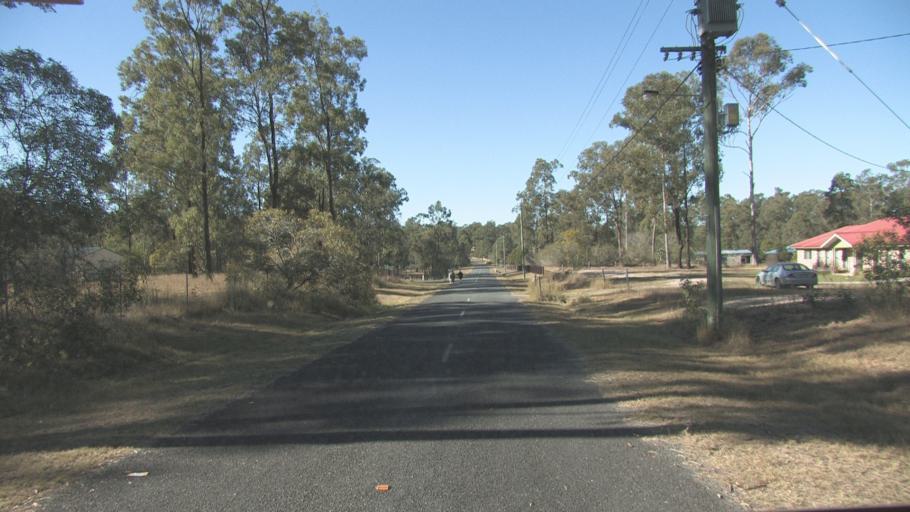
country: AU
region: Queensland
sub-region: Logan
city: North Maclean
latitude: -27.8098
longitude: 152.9651
